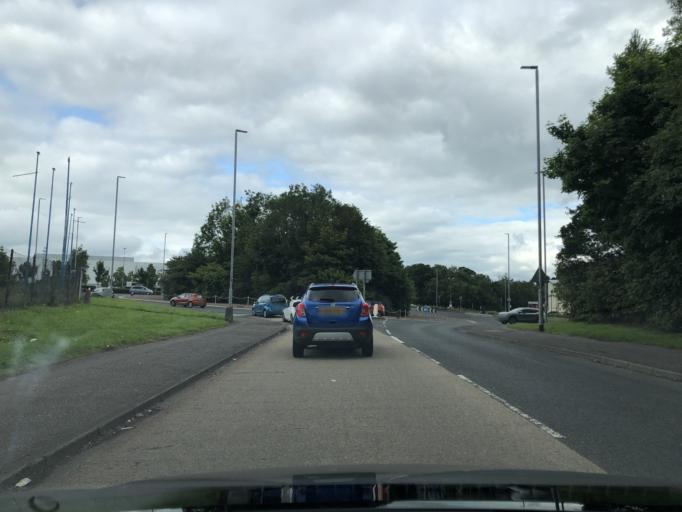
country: GB
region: Northern Ireland
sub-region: Newtownabbey District
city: Newtownabbey
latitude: 54.6560
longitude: -5.9217
